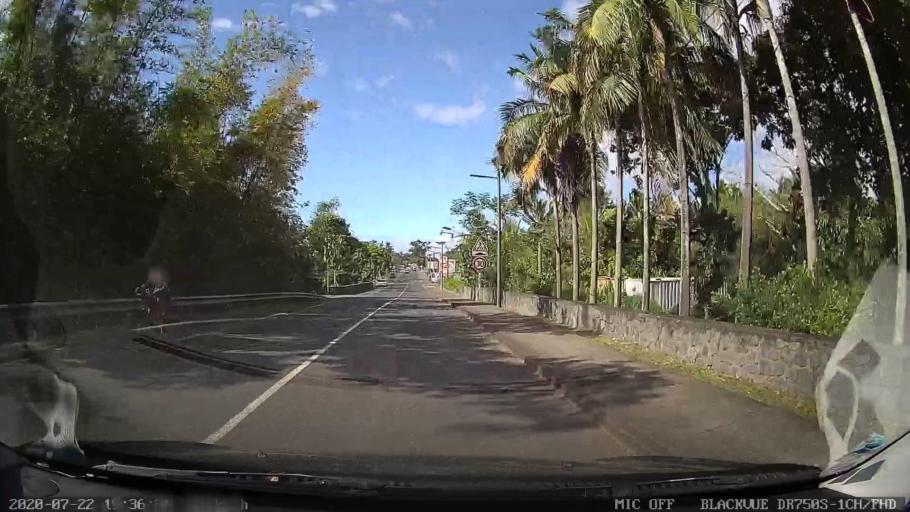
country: RE
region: Reunion
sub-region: Reunion
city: Sainte-Suzanne
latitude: -20.9083
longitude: 55.6092
